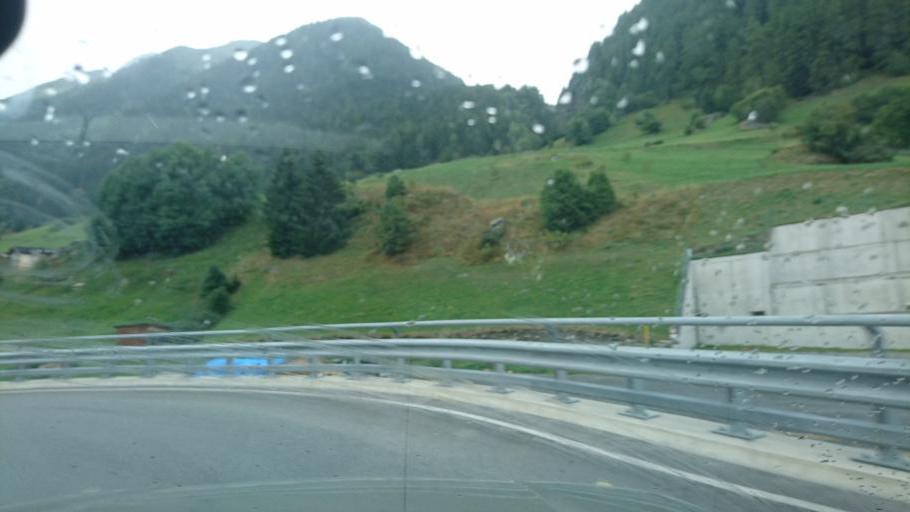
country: AT
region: Tyrol
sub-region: Politischer Bezirk Landeck
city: Ischgl
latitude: 47.0148
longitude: 10.2923
